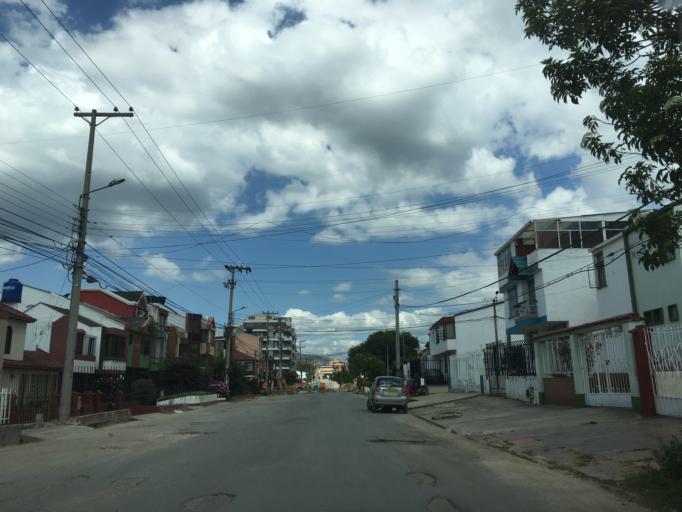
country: CO
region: Boyaca
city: Sogamoso
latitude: 5.7230
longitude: -72.9207
